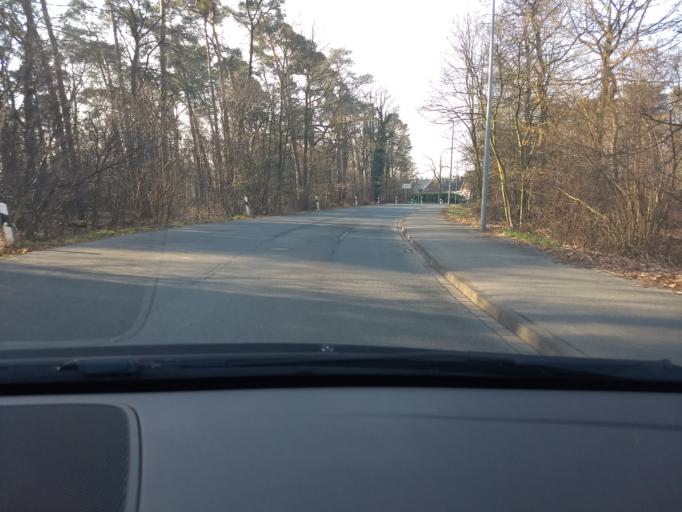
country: DE
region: North Rhine-Westphalia
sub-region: Regierungsbezirk Munster
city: Rhede
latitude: 51.8290
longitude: 6.7204
